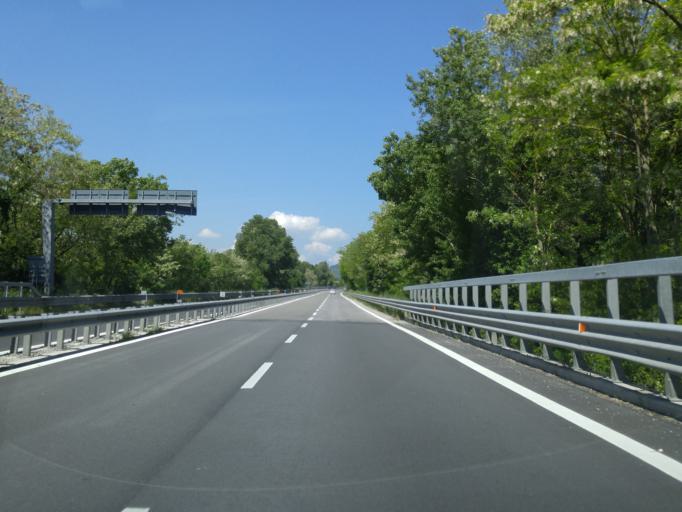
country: IT
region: The Marches
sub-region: Provincia di Pesaro e Urbino
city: Canavaccio
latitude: 43.6814
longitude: 12.7321
